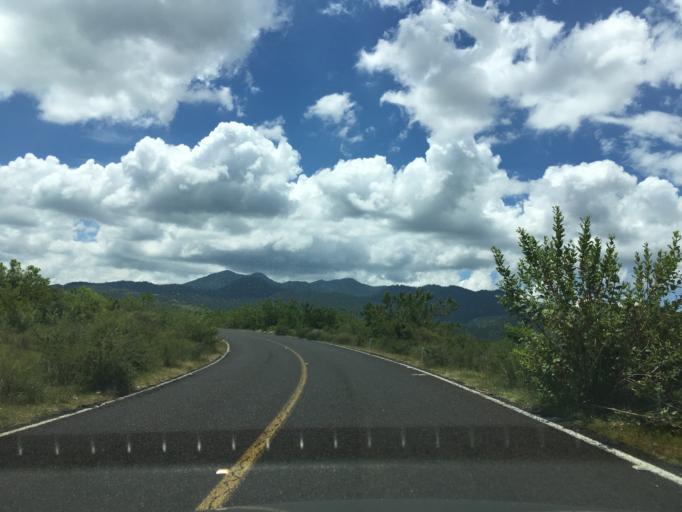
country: MX
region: Mexico
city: Huaniqueo de Morales
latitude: 19.7993
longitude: -101.4570
